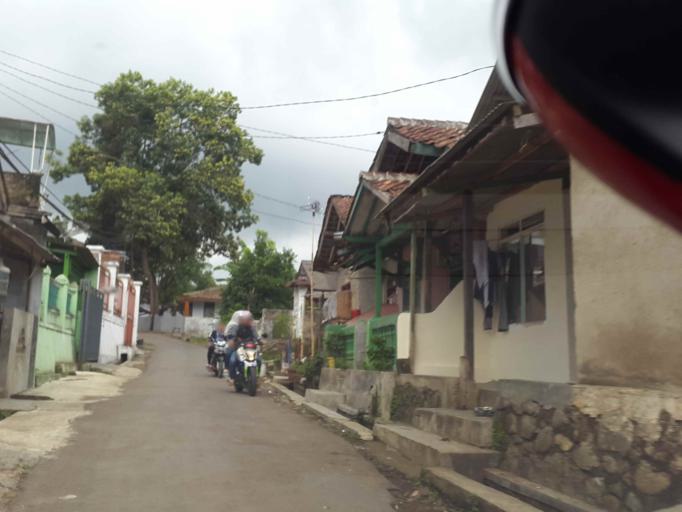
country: ID
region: West Java
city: Sukabumi
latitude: -6.9302
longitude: 106.9097
